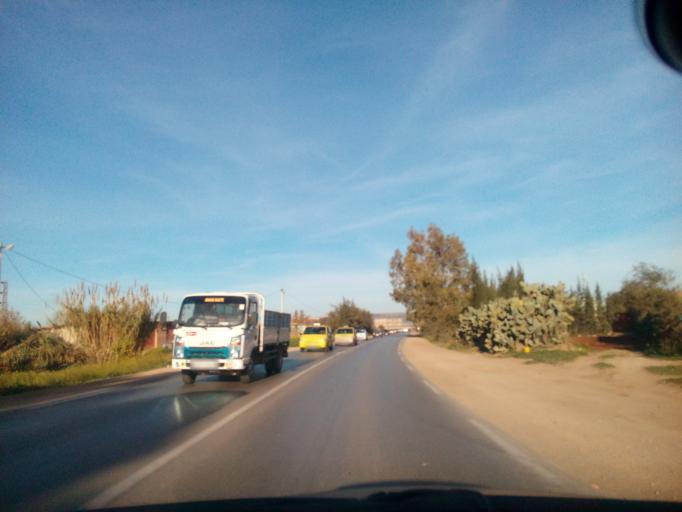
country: DZ
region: Mostaganem
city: Mostaganem
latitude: 35.7864
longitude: 0.1768
